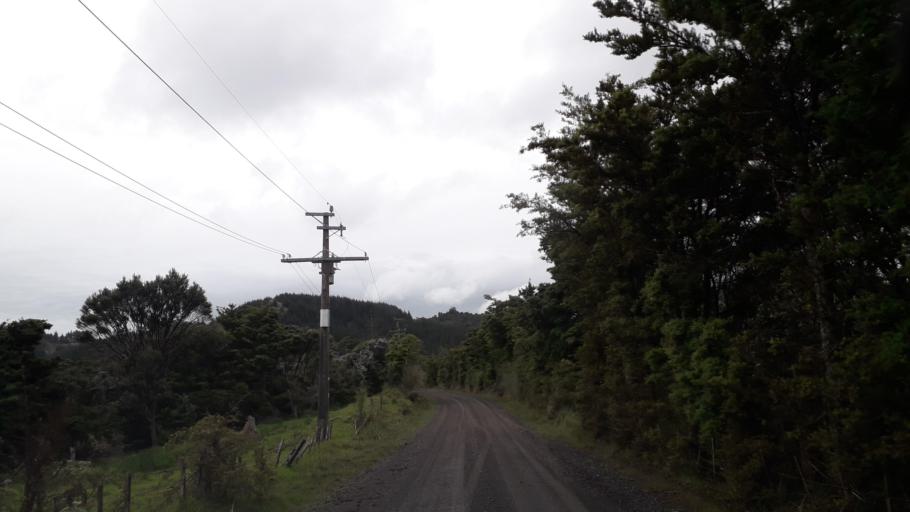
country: NZ
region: Northland
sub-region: Far North District
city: Kaitaia
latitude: -35.3792
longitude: 173.4104
